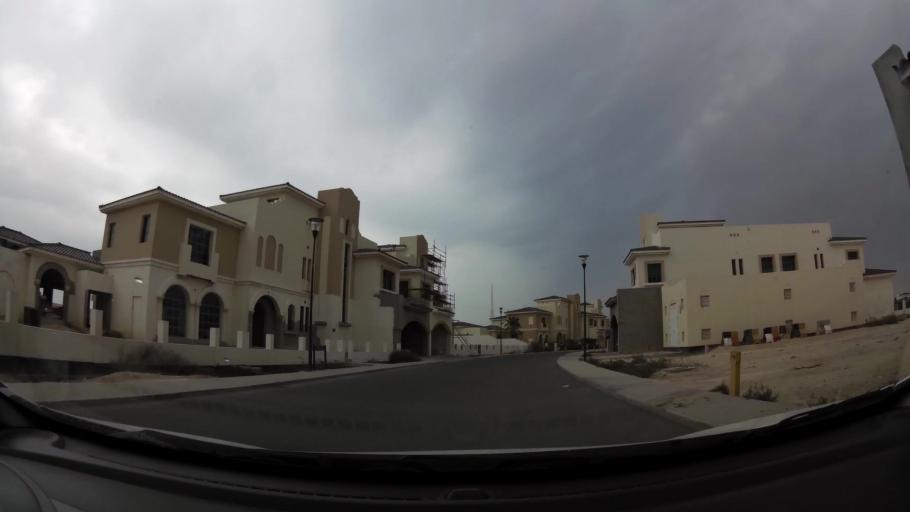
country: BH
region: Northern
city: Ar Rifa'
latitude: 26.0821
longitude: 50.5570
